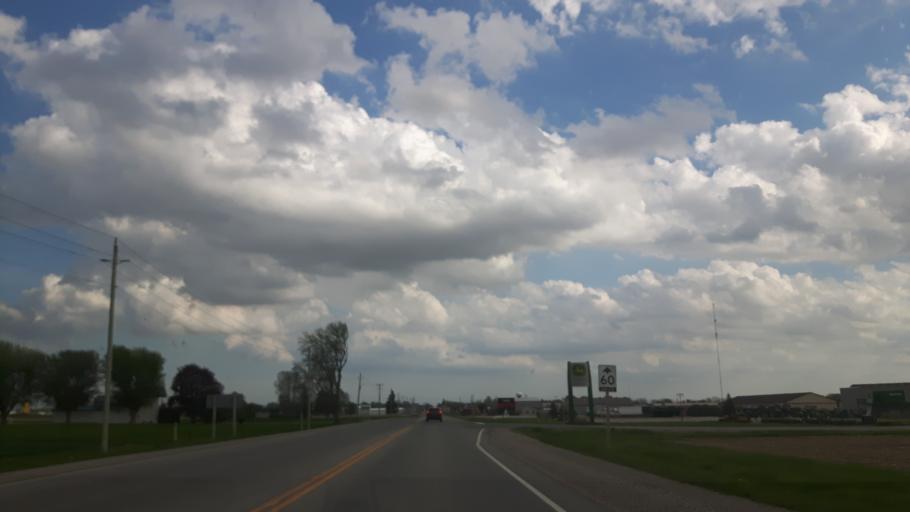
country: CA
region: Ontario
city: South Huron
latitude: 43.3696
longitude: -81.4852
